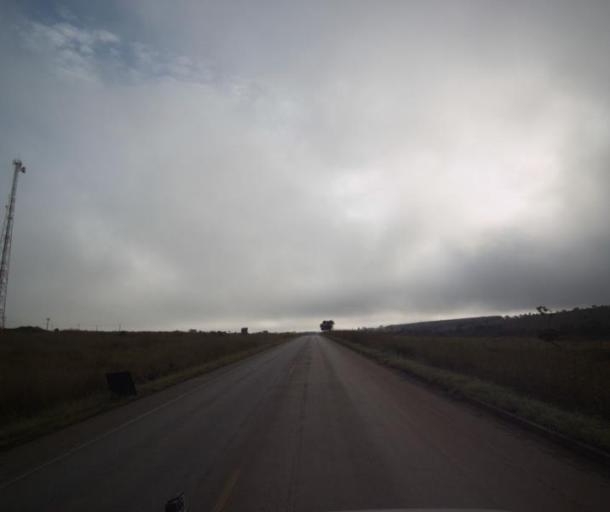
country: BR
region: Goias
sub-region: Pirenopolis
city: Pirenopolis
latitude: -15.7690
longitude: -48.7606
